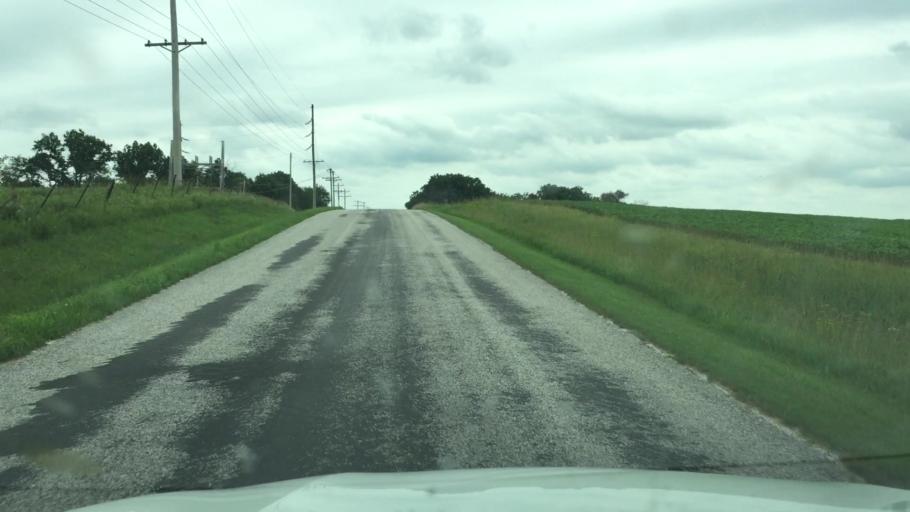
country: US
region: Illinois
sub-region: Hancock County
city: Carthage
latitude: 40.2970
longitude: -91.0832
